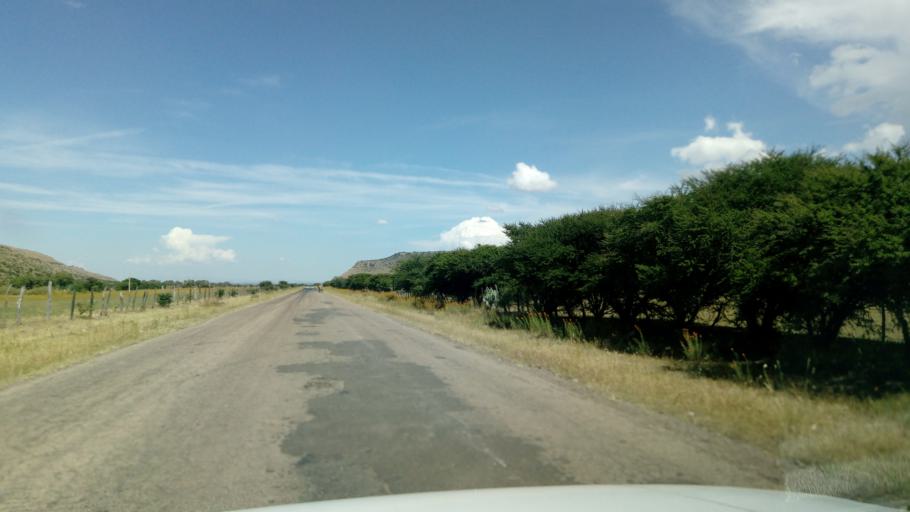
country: MX
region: Durango
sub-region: Durango
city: Jose Refugio Salcido
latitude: 23.8017
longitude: -104.4845
